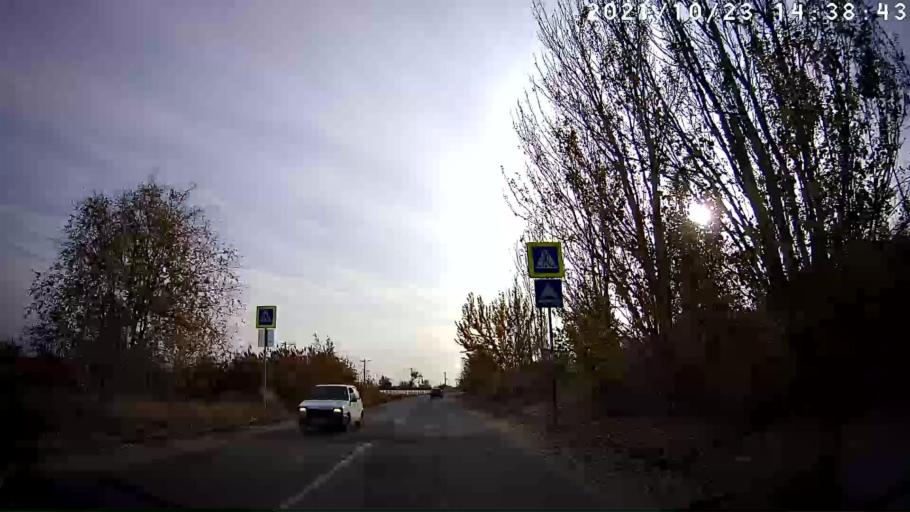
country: RU
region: Volgograd
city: Krasnoslobodsk
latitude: 48.4895
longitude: 44.5487
